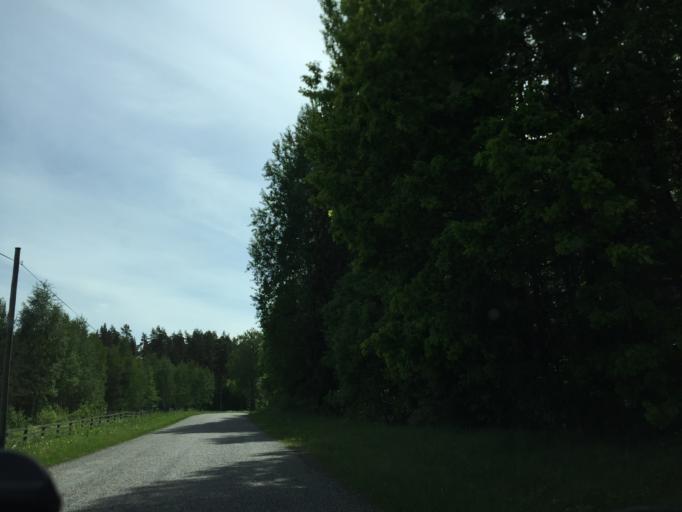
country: LV
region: Koceni
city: Koceni
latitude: 57.4922
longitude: 25.3634
